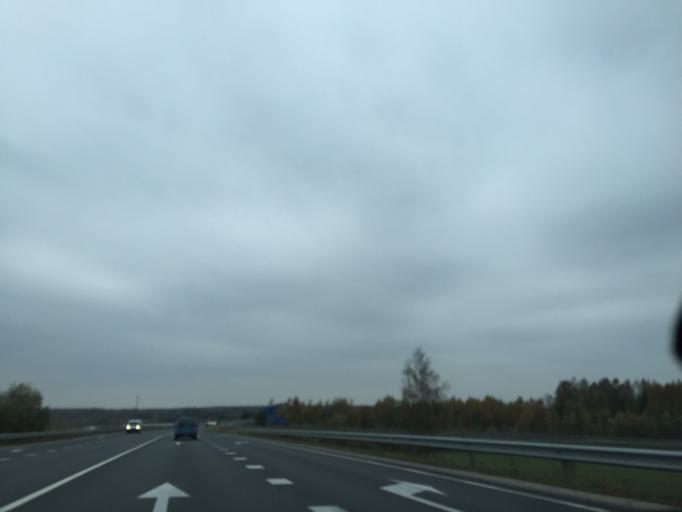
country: LV
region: Ozolnieku
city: Ozolnieki
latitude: 56.6508
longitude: 23.7997
